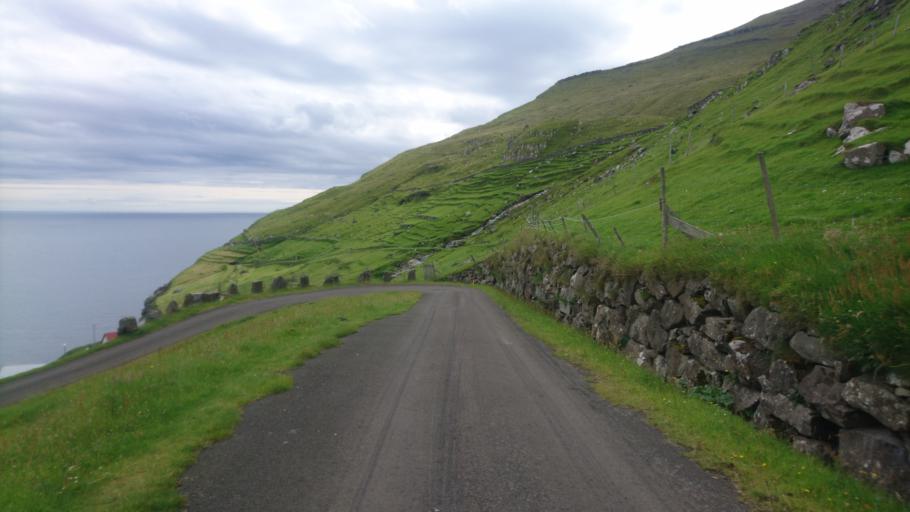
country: FO
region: Nordoyar
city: Klaksvik
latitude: 62.3303
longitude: -6.2780
